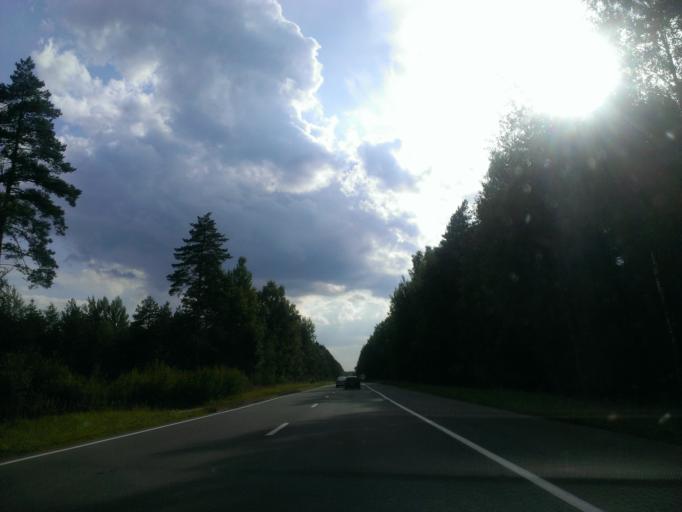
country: LV
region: Incukalns
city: Vangazi
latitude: 57.1006
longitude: 24.5830
